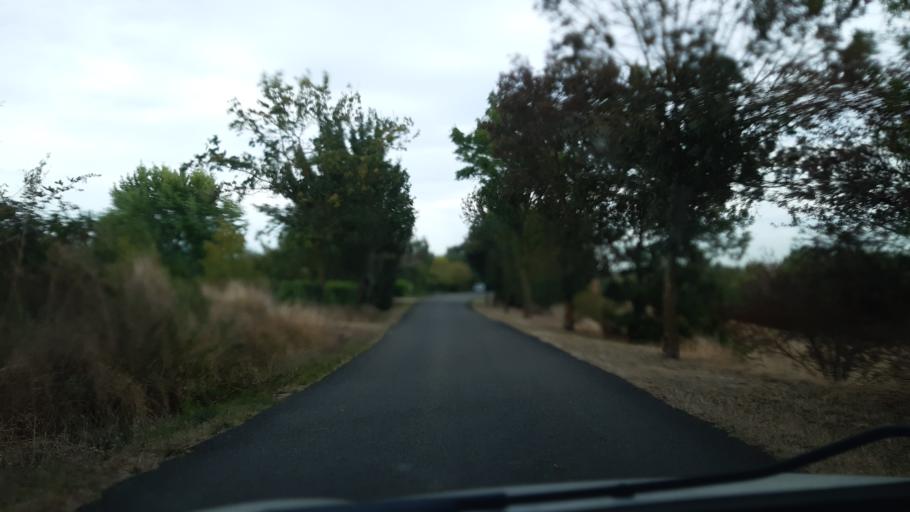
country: FR
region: Midi-Pyrenees
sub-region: Departement du Gers
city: Gimont
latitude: 43.6823
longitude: 0.9991
